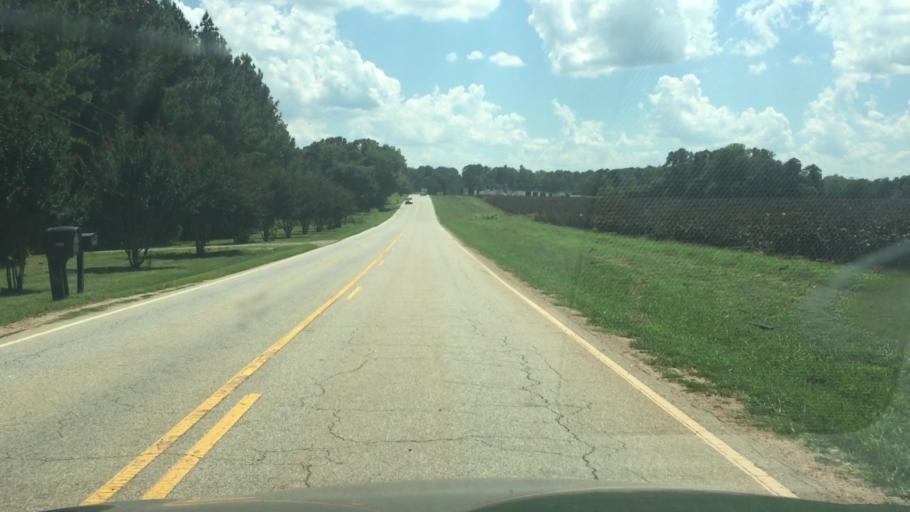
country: US
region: North Carolina
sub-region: Rowan County
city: Landis
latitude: 35.6202
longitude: -80.6499
